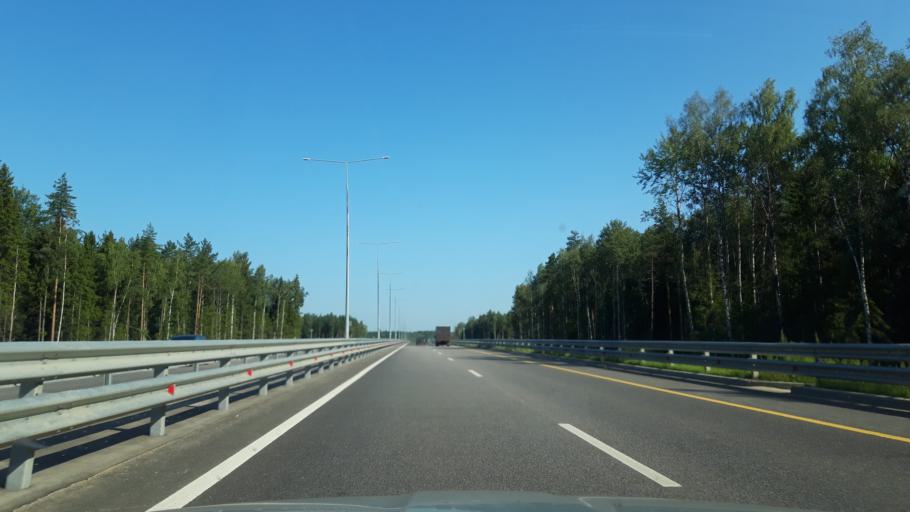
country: RU
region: Moskovskaya
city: Reshetnikovo
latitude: 56.4229
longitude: 36.5509
